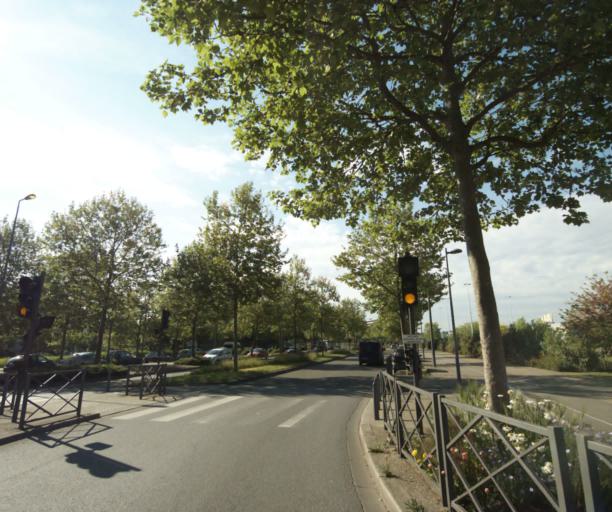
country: FR
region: Ile-de-France
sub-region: Departement des Yvelines
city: Les Mureaux
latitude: 48.9810
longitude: 1.9124
